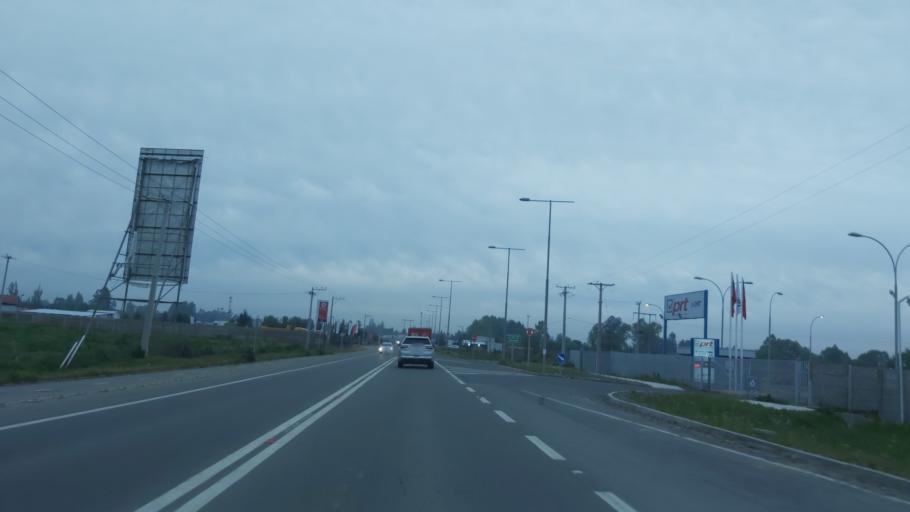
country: CL
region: Maule
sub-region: Provincia de Linares
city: Linares
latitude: -35.8345
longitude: -71.6208
